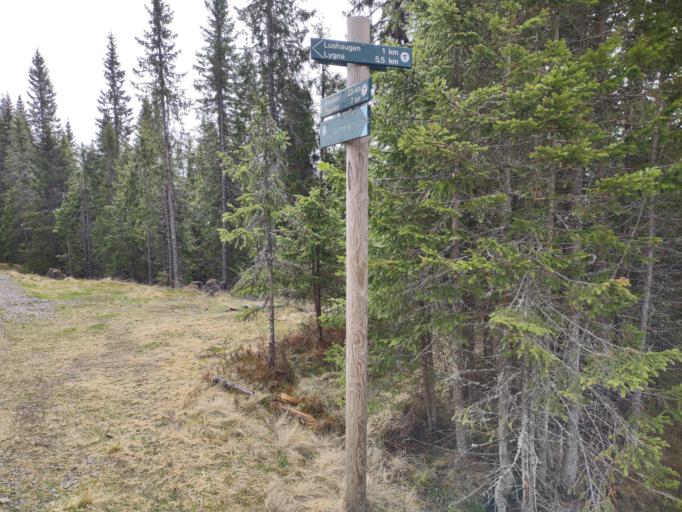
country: NO
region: Oppland
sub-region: Gran
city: Jaren
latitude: 60.4206
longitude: 10.6867
